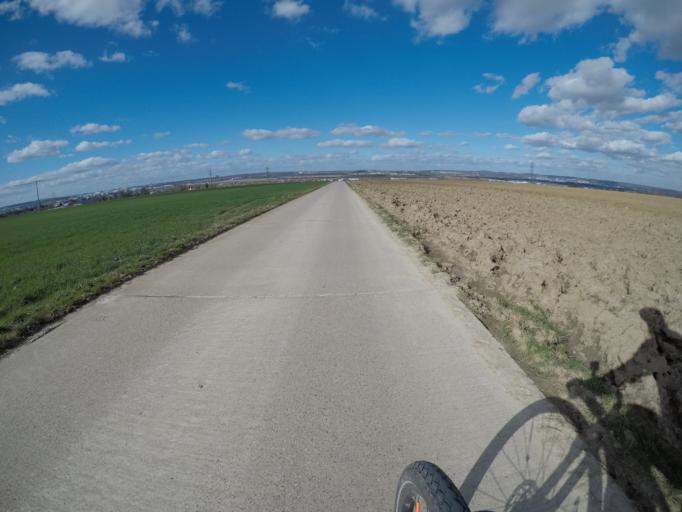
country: DE
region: Baden-Wuerttemberg
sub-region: Regierungsbezirk Stuttgart
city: Filderstadt
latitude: 48.6613
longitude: 9.2484
